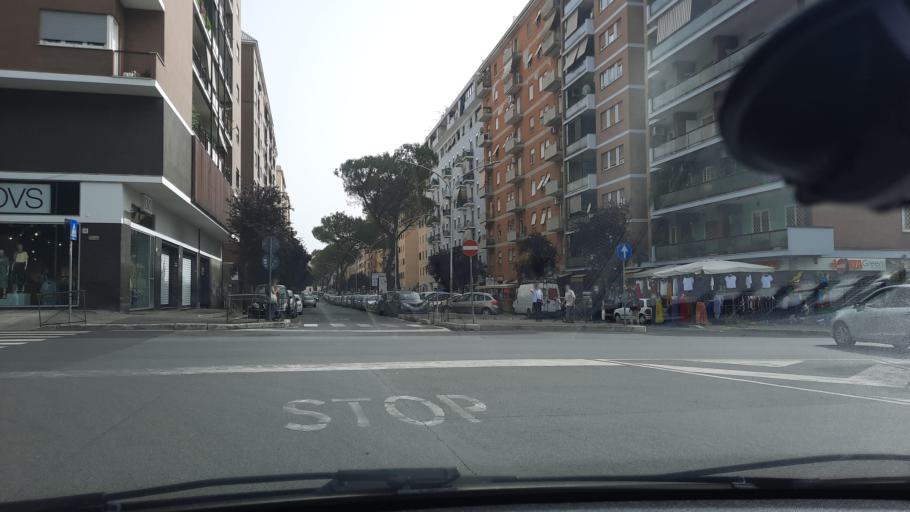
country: IT
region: Latium
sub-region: Citta metropolitana di Roma Capitale
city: Rome
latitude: 41.8567
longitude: 12.4801
